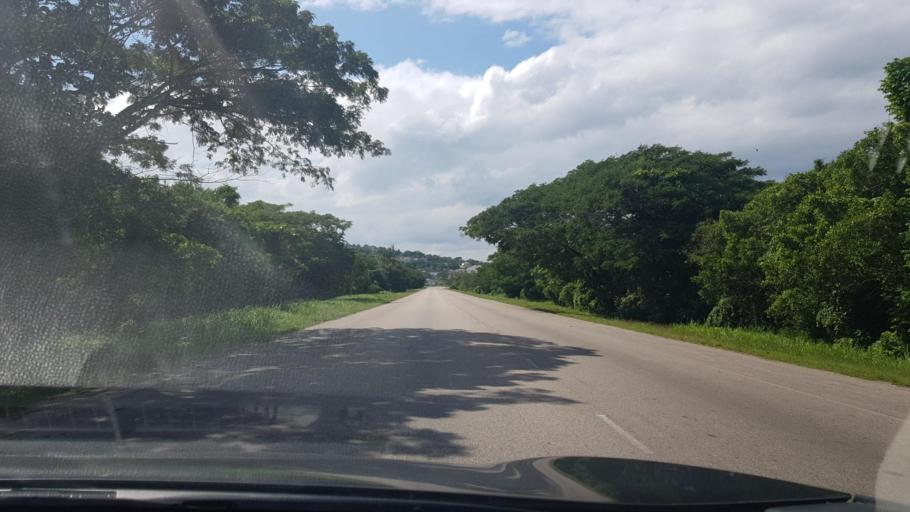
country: JM
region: Trelawny
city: Falmouth
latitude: 18.4768
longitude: -77.6381
